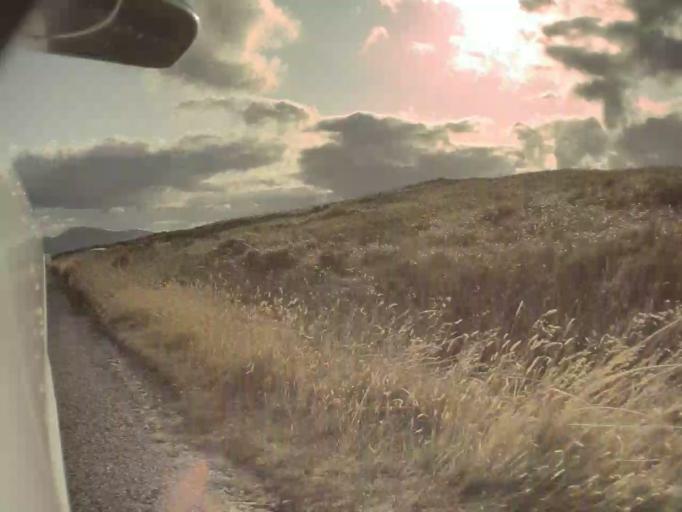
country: IE
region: Leinster
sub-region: Wicklow
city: Enniskerry
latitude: 53.1179
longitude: -6.3013
